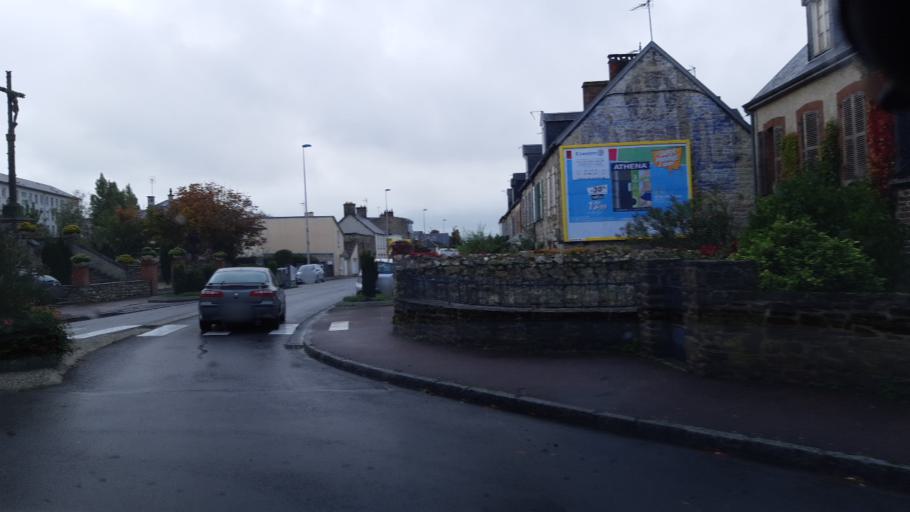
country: FR
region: Lower Normandy
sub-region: Departement de la Manche
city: Donville-les-Bains
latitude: 48.8526
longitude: -1.5683
